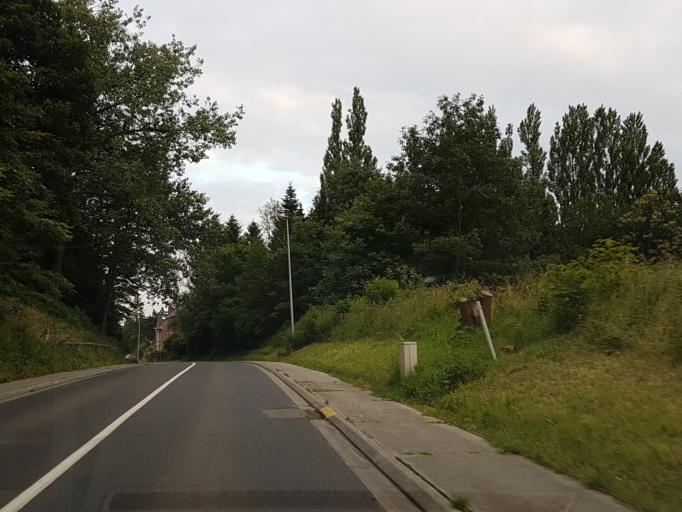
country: BE
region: Flanders
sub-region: Provincie Vlaams-Brabant
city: Ternat
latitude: 50.9076
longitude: 4.1300
